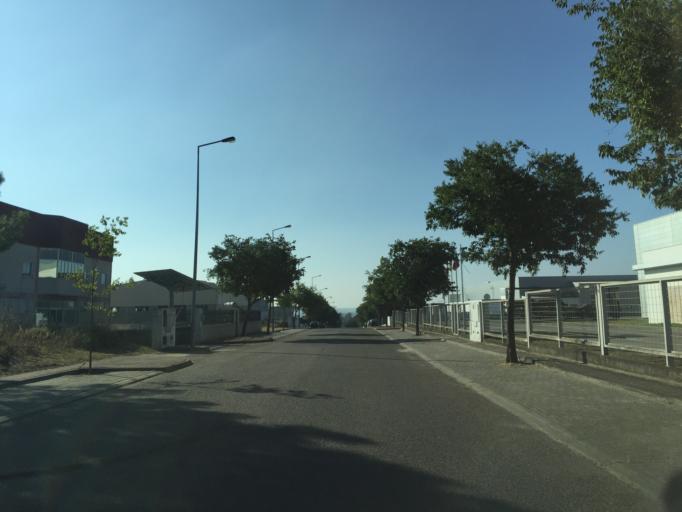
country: PT
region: Santarem
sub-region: Abrantes
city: Alferrarede
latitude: 39.4916
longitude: -8.1860
